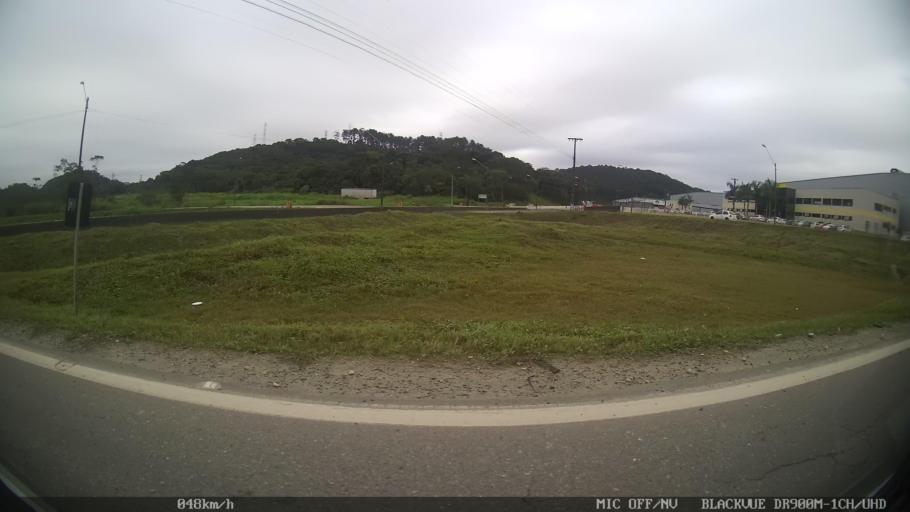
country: BR
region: Santa Catarina
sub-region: Joinville
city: Joinville
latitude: -26.2579
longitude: -48.9033
